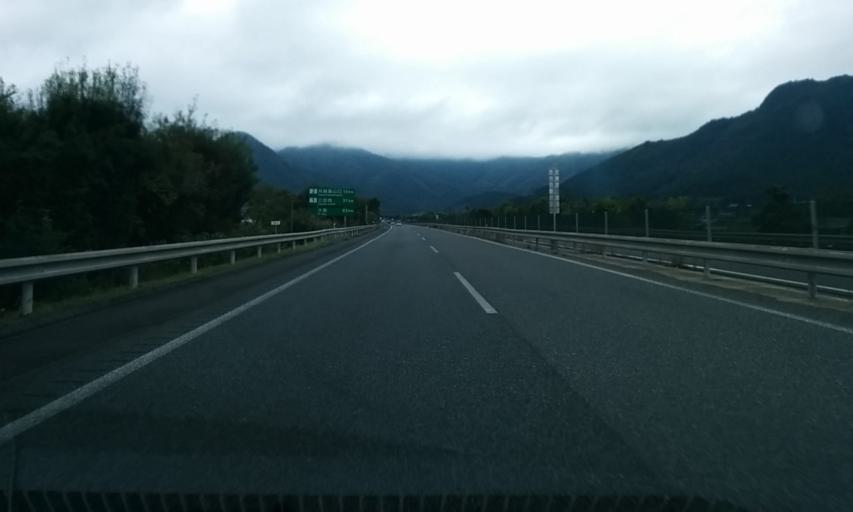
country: JP
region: Hyogo
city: Sasayama
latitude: 35.1546
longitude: 135.1217
